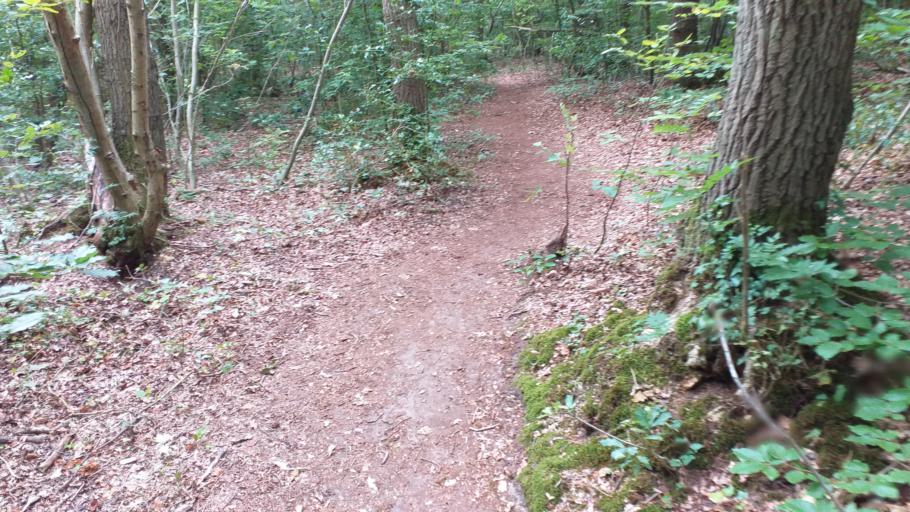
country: NL
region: North Holland
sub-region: Gemeente Heiloo
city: Heiloo
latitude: 52.6735
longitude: 4.6855
